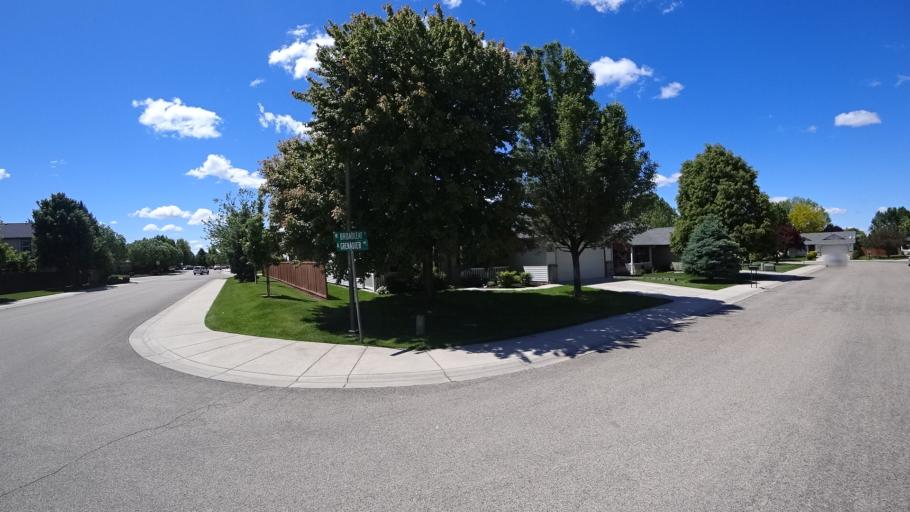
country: US
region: Idaho
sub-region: Ada County
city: Meridian
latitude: 43.6351
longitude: -116.3431
